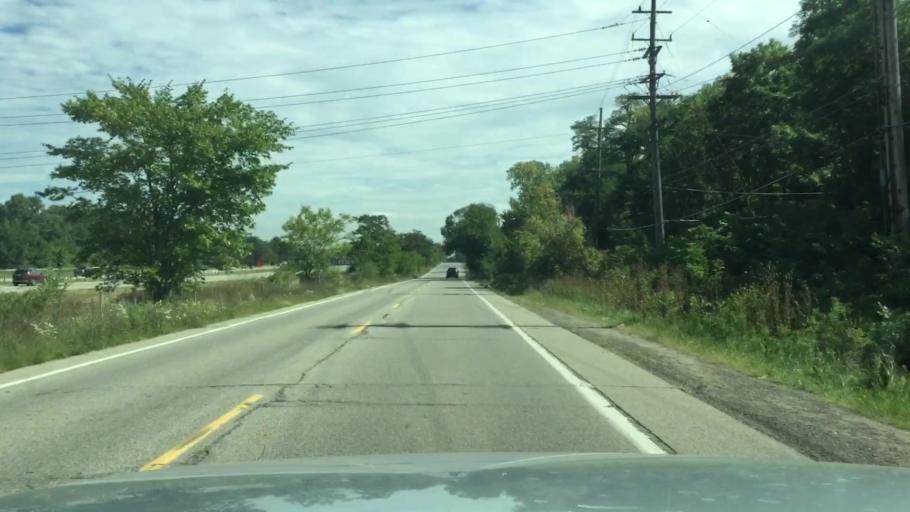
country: US
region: Michigan
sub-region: Wayne County
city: Belleville
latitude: 42.2187
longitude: -83.5046
